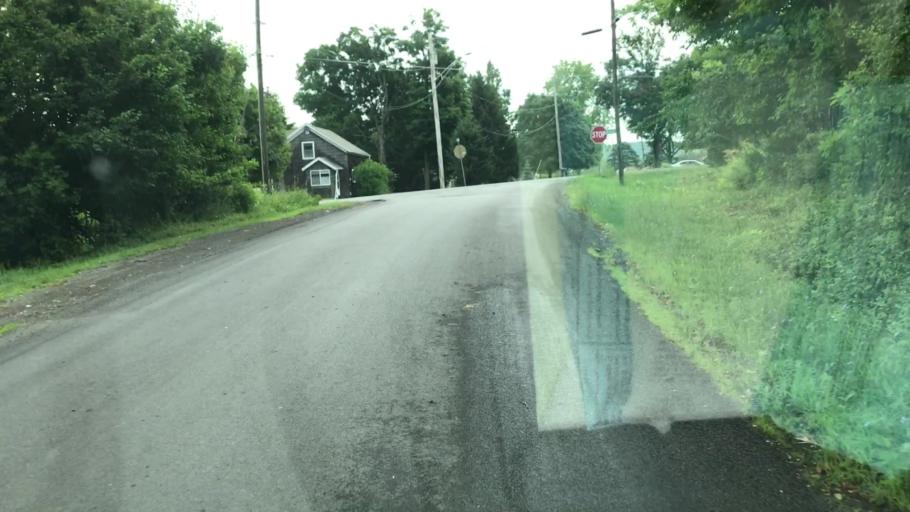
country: US
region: New York
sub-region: Onondaga County
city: Manlius
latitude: 42.9798
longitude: -75.9832
